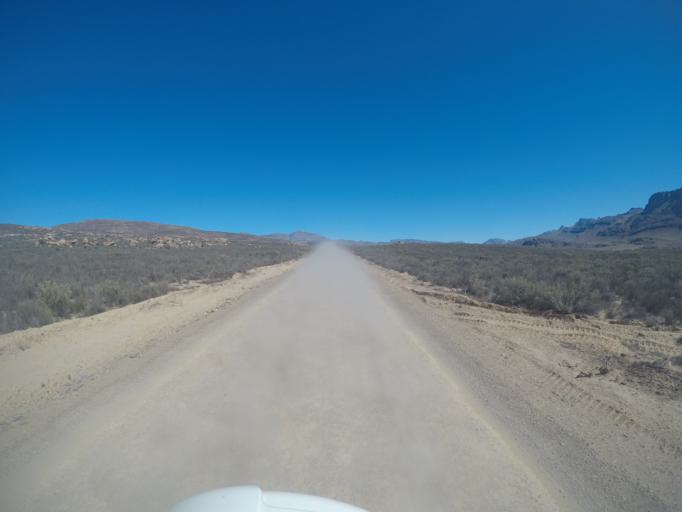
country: ZA
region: Western Cape
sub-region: West Coast District Municipality
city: Clanwilliam
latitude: -32.5054
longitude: 19.2930
